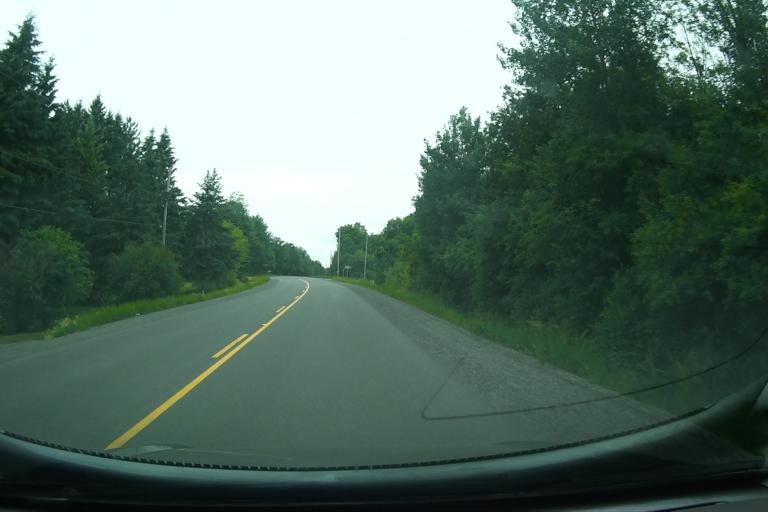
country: CA
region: Ontario
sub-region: Lanark County
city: Smiths Falls
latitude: 44.9733
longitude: -75.7823
